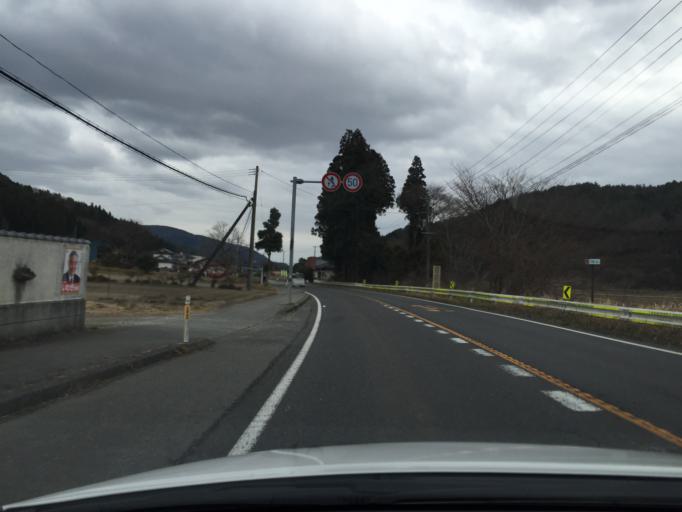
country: JP
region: Fukushima
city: Iwaki
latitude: 37.1223
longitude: 140.7375
